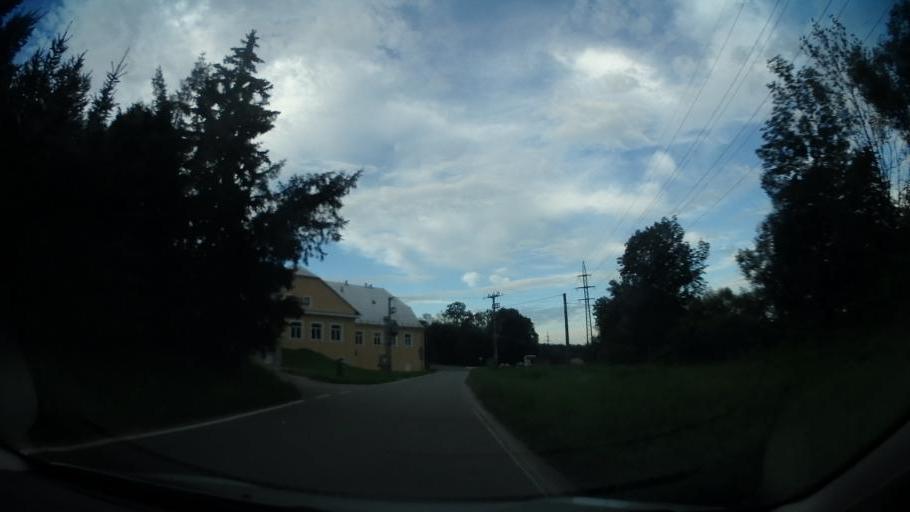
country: CZ
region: Olomoucky
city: Cervenka
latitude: 49.7202
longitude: 17.0303
